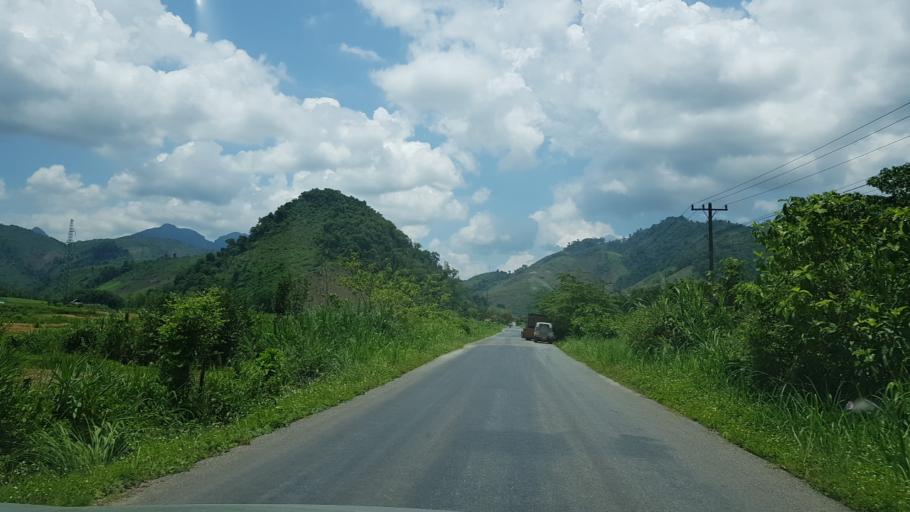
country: LA
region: Vientiane
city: Muang Kasi
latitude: 19.1299
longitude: 102.2708
